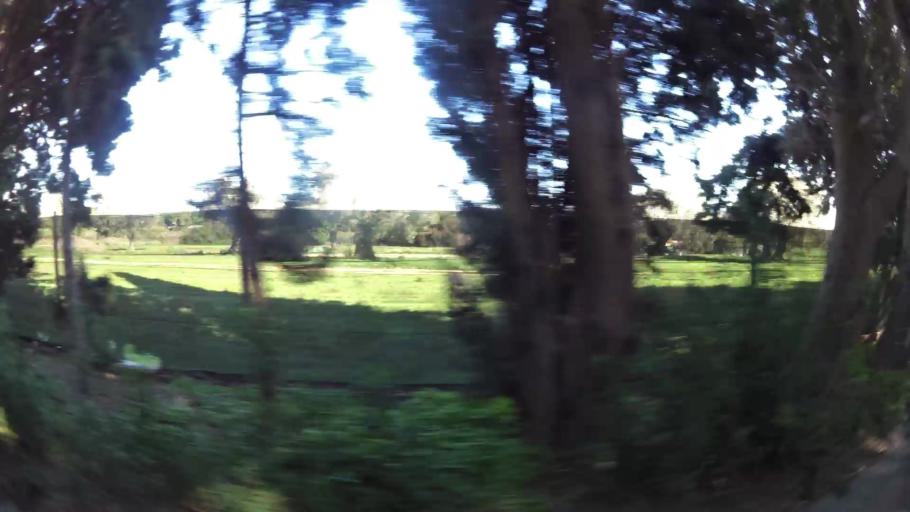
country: GR
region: Attica
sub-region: Nomarchia Anatolikis Attikis
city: Pikermi
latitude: 38.0090
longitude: 23.9370
